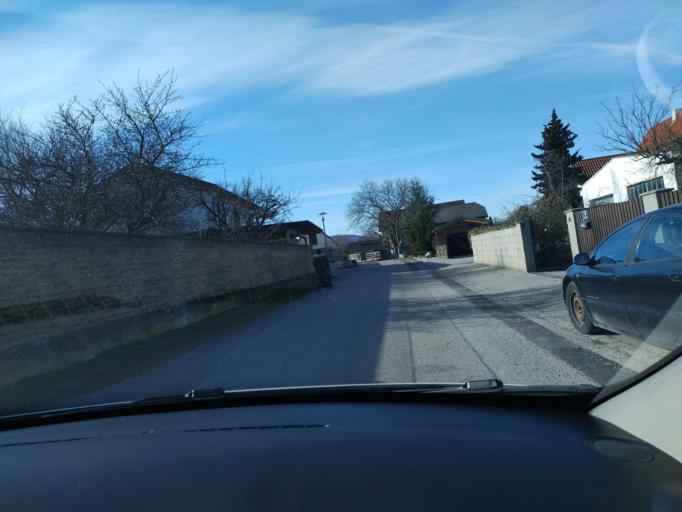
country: AT
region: Lower Austria
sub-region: Politischer Bezirk Wiener Neustadt
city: Lanzenkirchen
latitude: 47.7421
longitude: 16.2371
